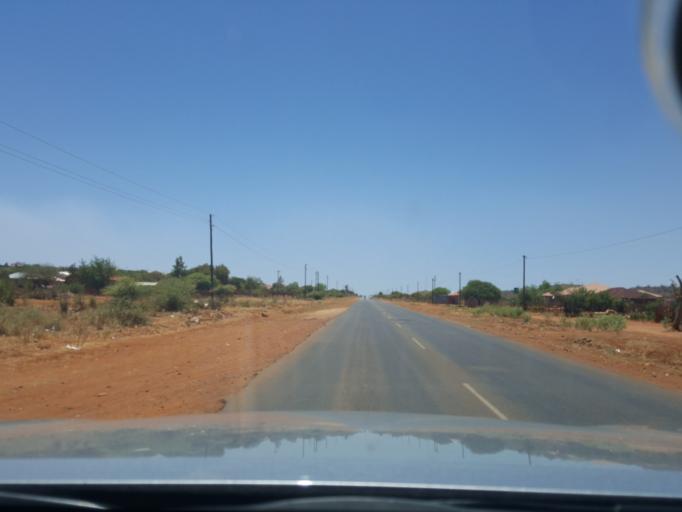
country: ZA
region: North-West
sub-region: Ngaka Modiri Molema District Municipality
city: Zeerust
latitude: -25.4554
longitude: 25.9691
